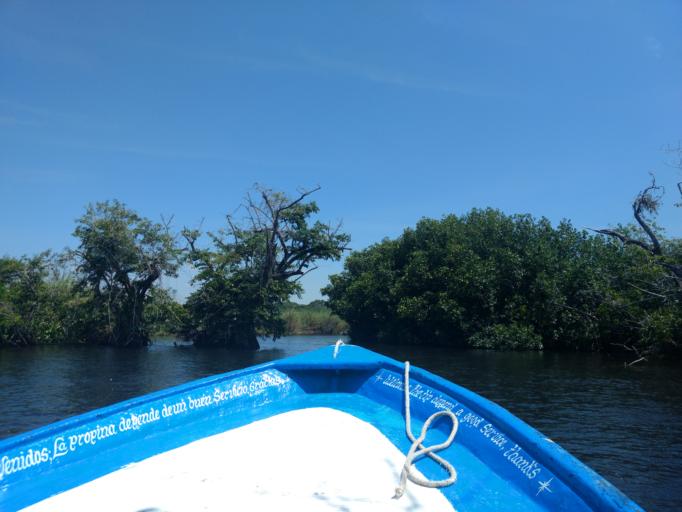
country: MX
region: Nayarit
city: San Blas
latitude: 21.5357
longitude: -105.2369
